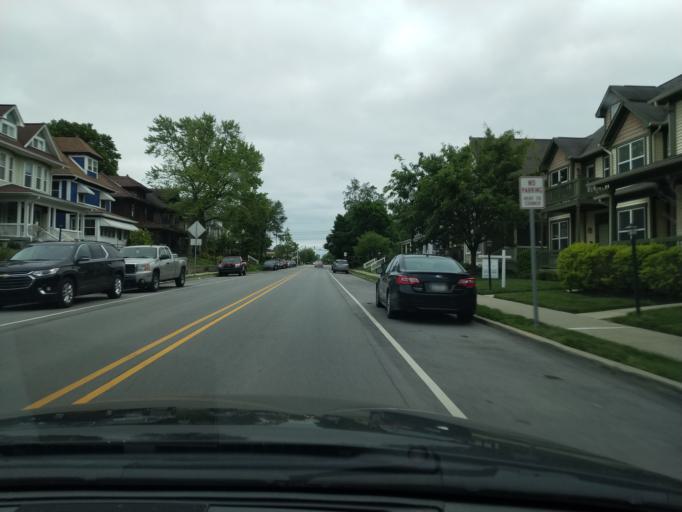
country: US
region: Indiana
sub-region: Marion County
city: Indianapolis
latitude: 39.7992
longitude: -86.1495
